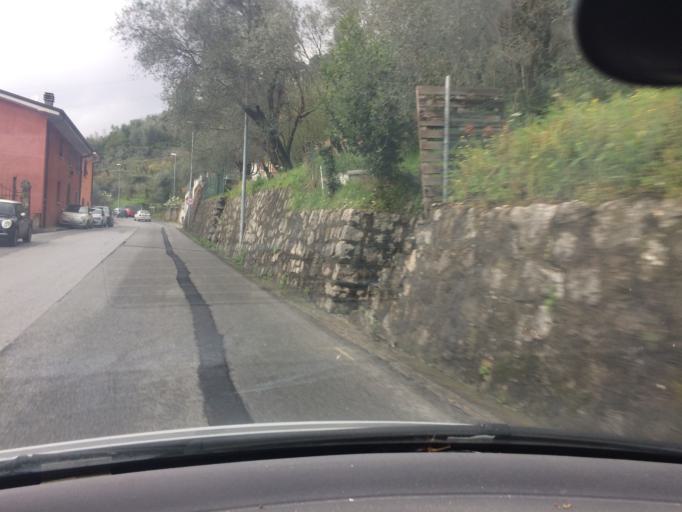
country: IT
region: Tuscany
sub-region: Provincia di Massa-Carrara
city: Massa
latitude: 44.0501
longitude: 10.1292
